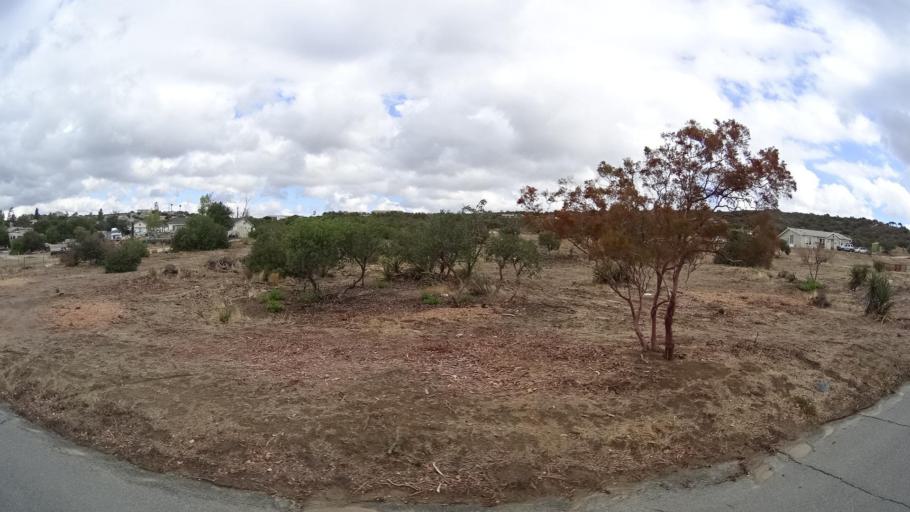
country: US
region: California
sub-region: San Diego County
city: Campo
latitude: 32.6300
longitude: -116.4208
